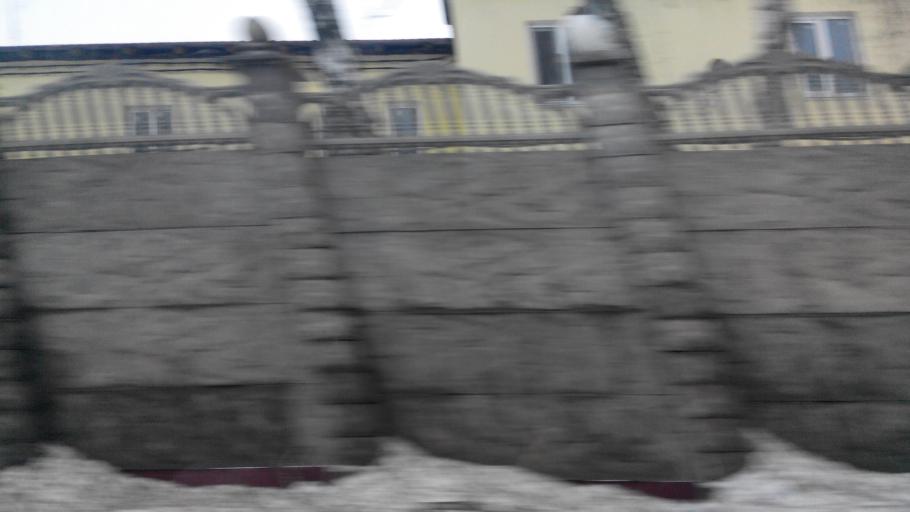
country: RU
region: Tula
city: Mayskiy
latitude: 53.9794
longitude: 38.2283
